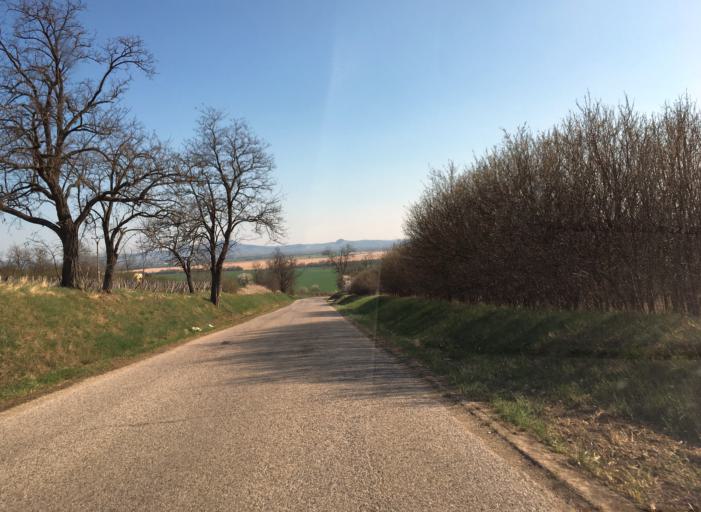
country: HU
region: Komarom-Esztergom
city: Nyergesujfalu
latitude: 47.8234
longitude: 18.6031
